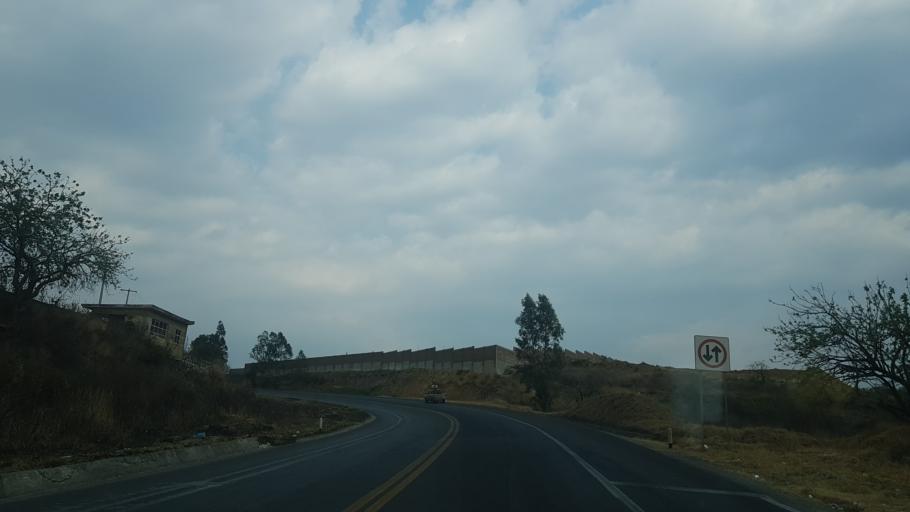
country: MX
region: Puebla
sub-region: Santa Isabel Cholula
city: San Pablo Ahuatempa
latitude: 18.9753
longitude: -98.3753
